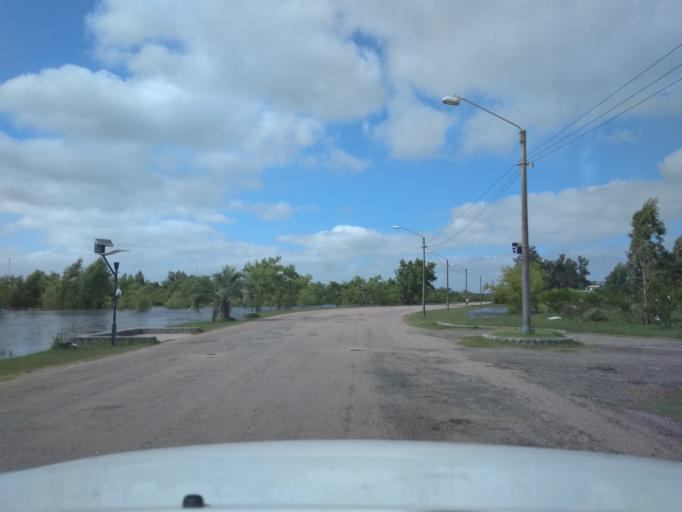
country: UY
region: Florida
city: Florida
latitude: -34.1036
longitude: -56.2038
